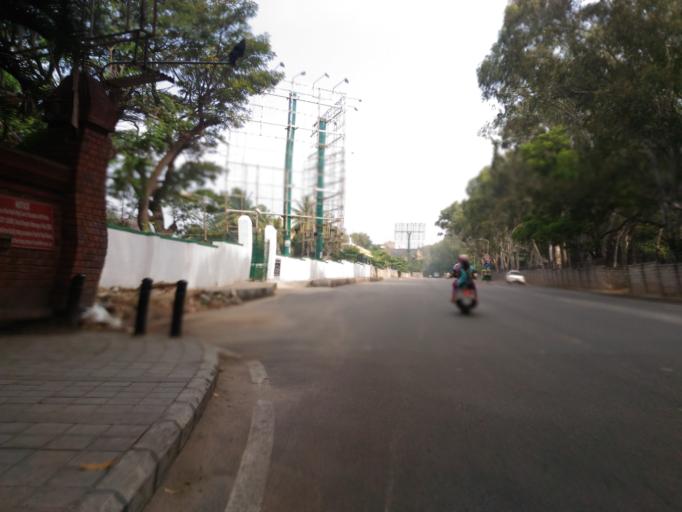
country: IN
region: Karnataka
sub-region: Bangalore Urban
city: Bangalore
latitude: 12.9587
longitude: 77.6061
